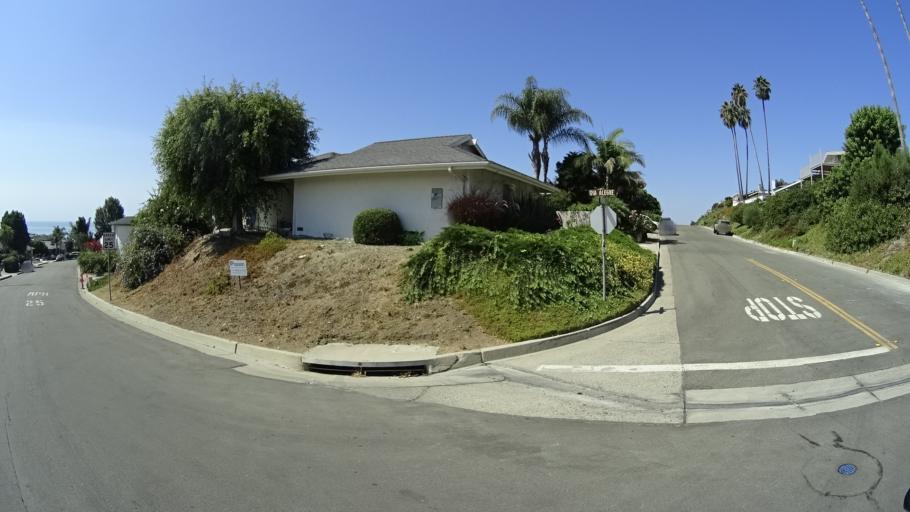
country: US
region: California
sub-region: Orange County
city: San Clemente
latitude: 33.4451
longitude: -117.6381
